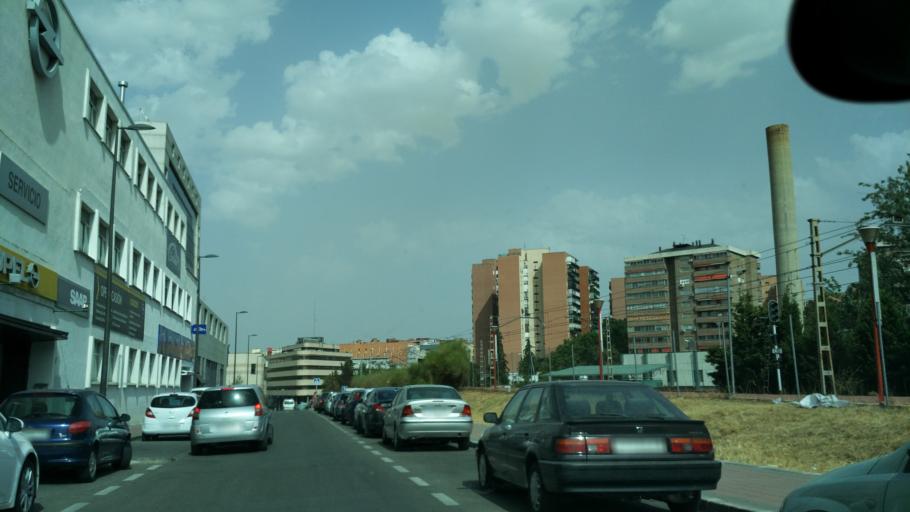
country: ES
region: Madrid
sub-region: Provincia de Madrid
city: Pinar de Chamartin
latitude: 40.4883
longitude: -3.6934
